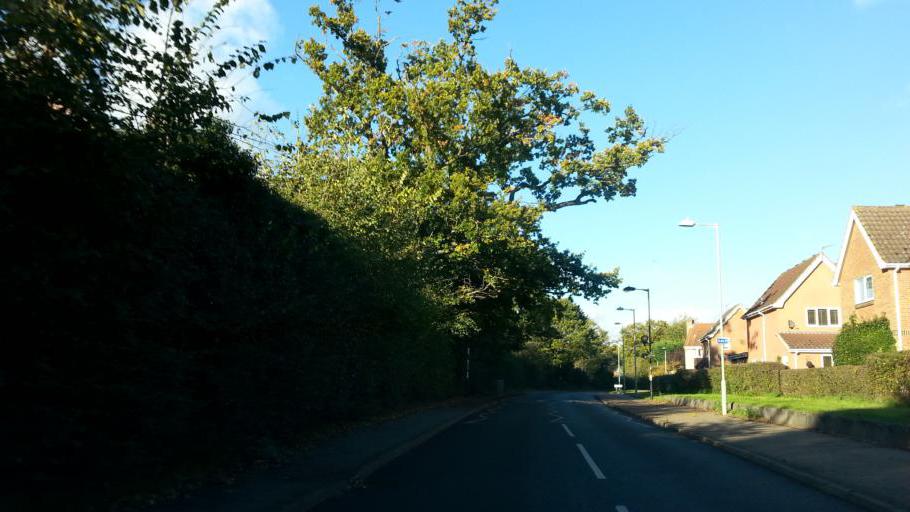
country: GB
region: England
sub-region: Suffolk
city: Thurston
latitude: 52.2517
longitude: 0.8106
